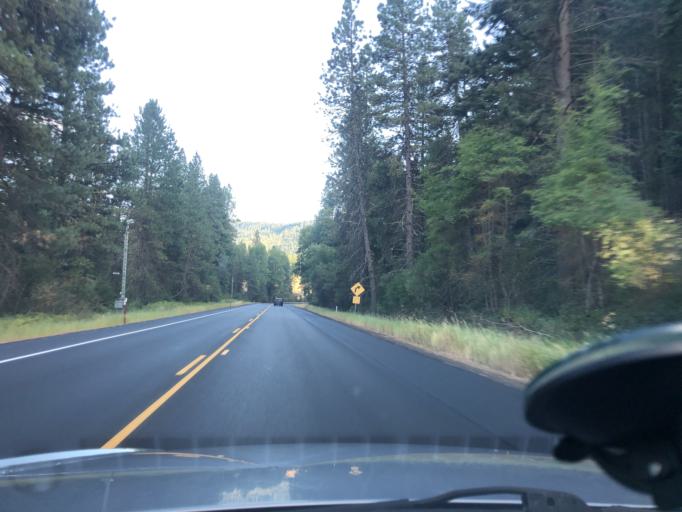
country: US
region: Washington
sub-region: Kittitas County
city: Cle Elum
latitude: 47.2535
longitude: -120.6939
